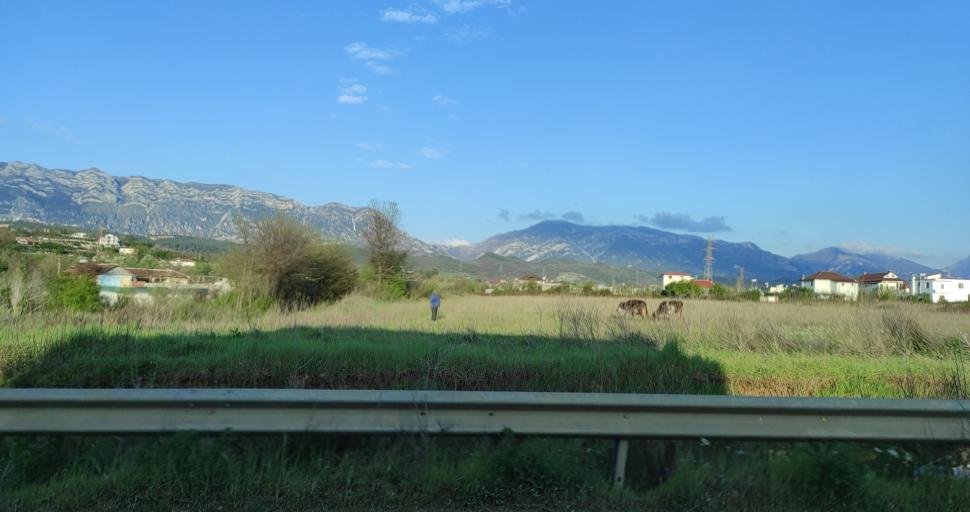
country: AL
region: Durres
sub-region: Rrethi i Krujes
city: Fushe-Kruje
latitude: 41.4817
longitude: 19.7344
